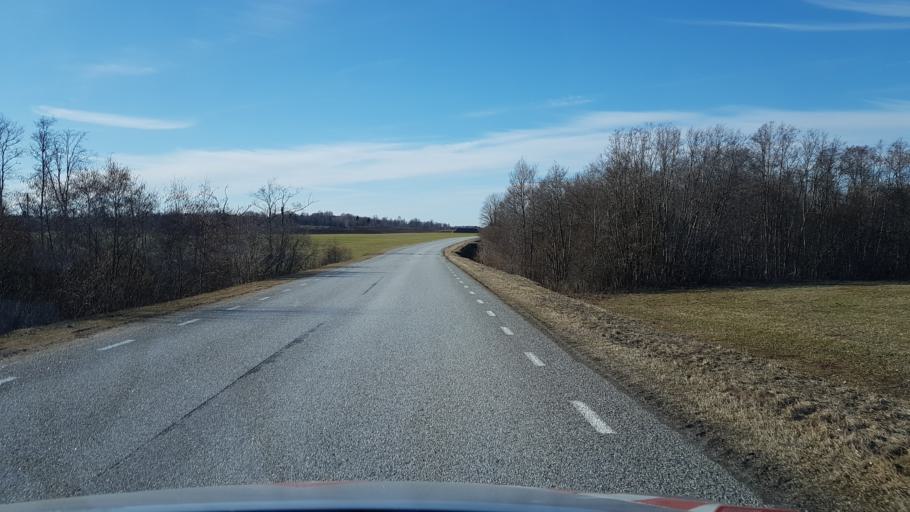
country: EE
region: Laeaene-Virumaa
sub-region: Kadrina vald
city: Kadrina
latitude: 59.2976
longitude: 26.1662
